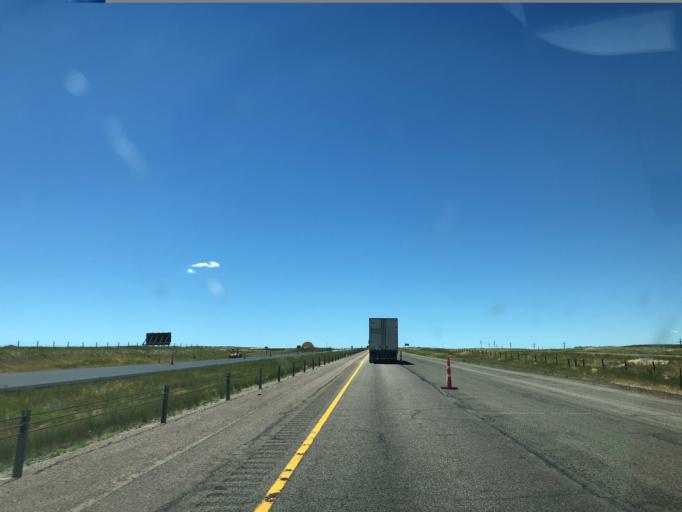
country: US
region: Wyoming
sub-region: Laramie County
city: Cheyenne
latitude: 41.0990
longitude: -105.1400
